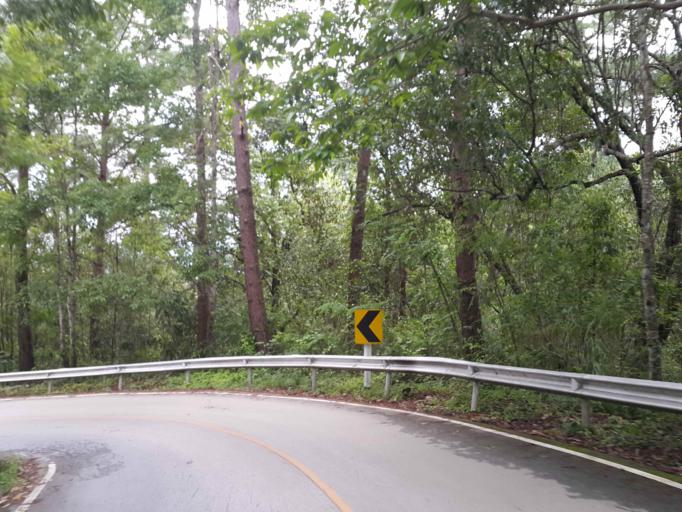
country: TH
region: Chiang Mai
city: Mae Chaem
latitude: 18.5155
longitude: 98.4507
